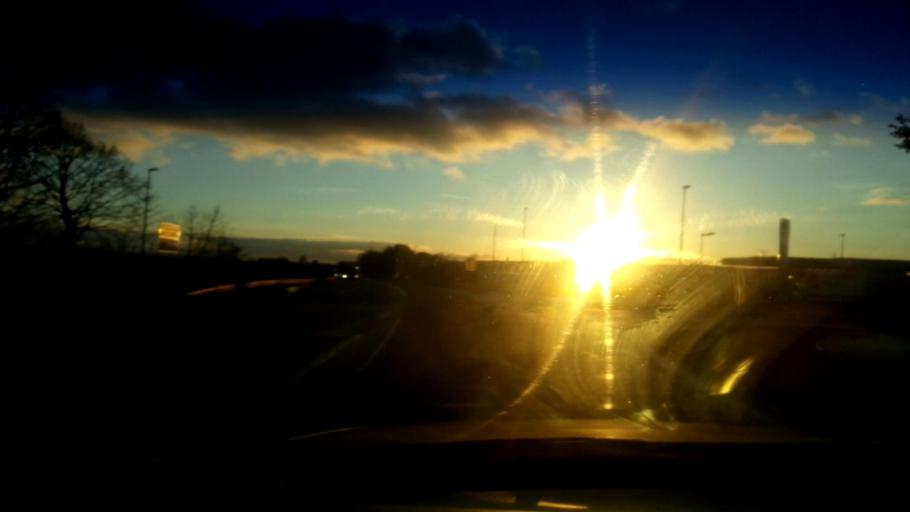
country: DE
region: Bavaria
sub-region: Upper Franconia
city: Buttenheim
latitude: 49.7982
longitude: 11.0292
